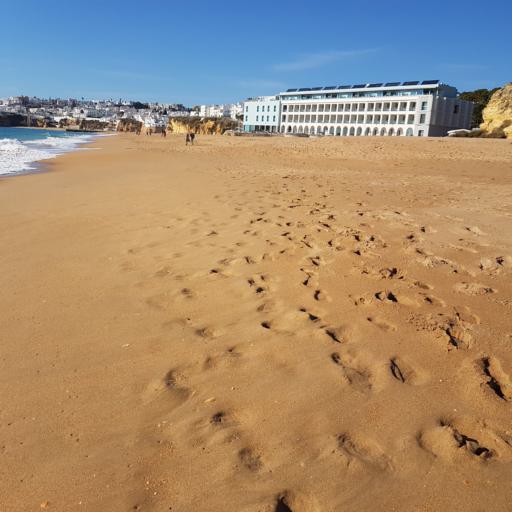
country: PT
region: Faro
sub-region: Albufeira
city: Albufeira
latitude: 37.0849
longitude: -8.2418
